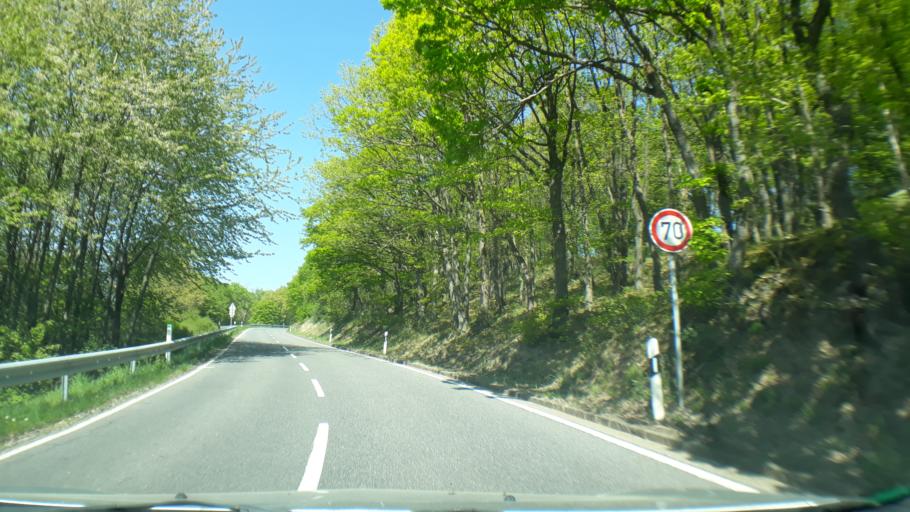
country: DE
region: North Rhine-Westphalia
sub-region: Regierungsbezirk Koln
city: Nideggen
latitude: 50.6859
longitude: 6.4316
